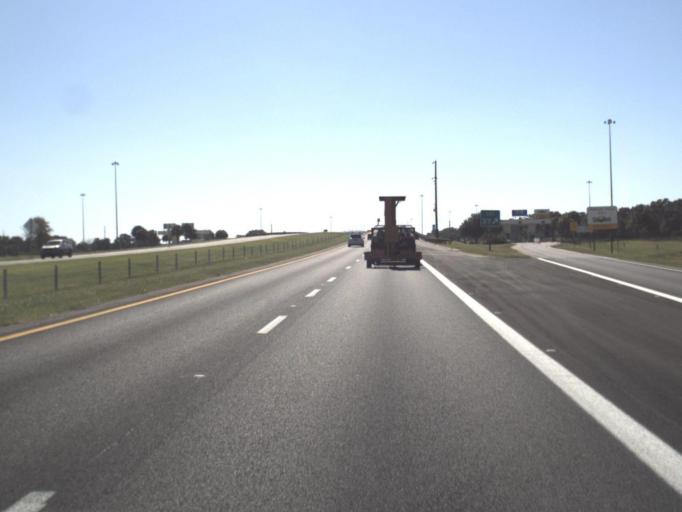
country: US
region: Florida
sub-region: Hernando County
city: Masaryktown
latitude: 28.4387
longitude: -82.4852
